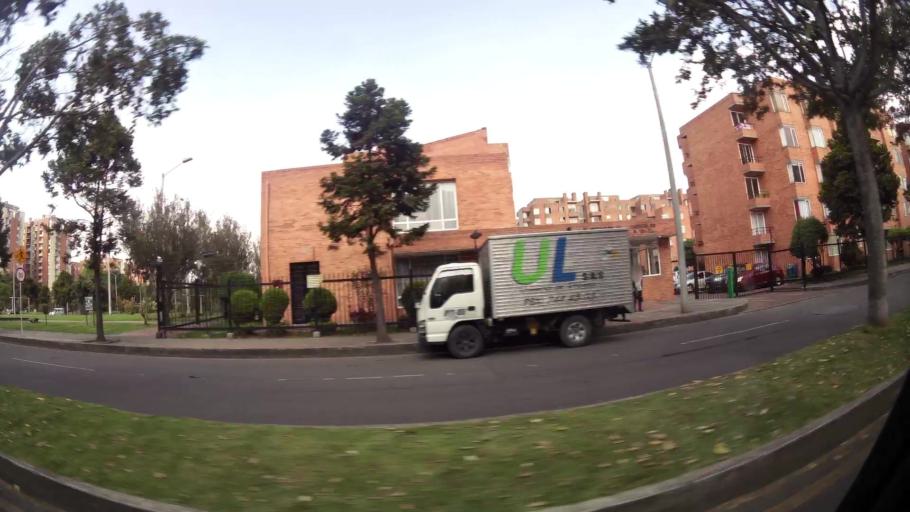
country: CO
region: Bogota D.C.
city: Barrio San Luis
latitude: 4.7354
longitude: -74.0600
